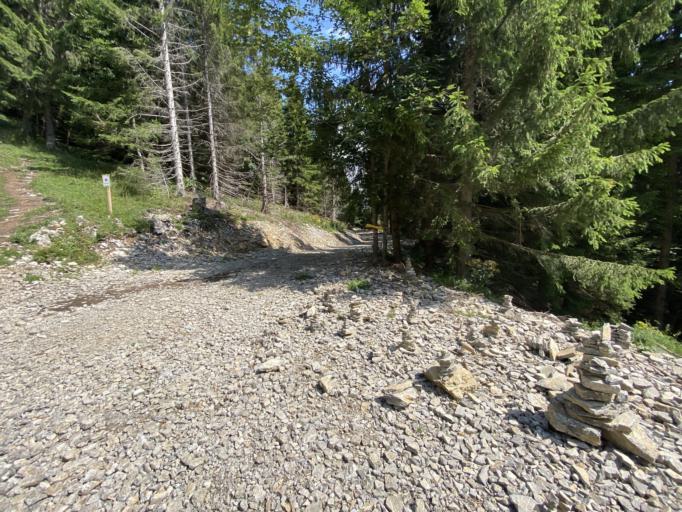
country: AT
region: Lower Austria
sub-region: Politischer Bezirk Lilienfeld
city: Annaberg
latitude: 47.8911
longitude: 15.3608
